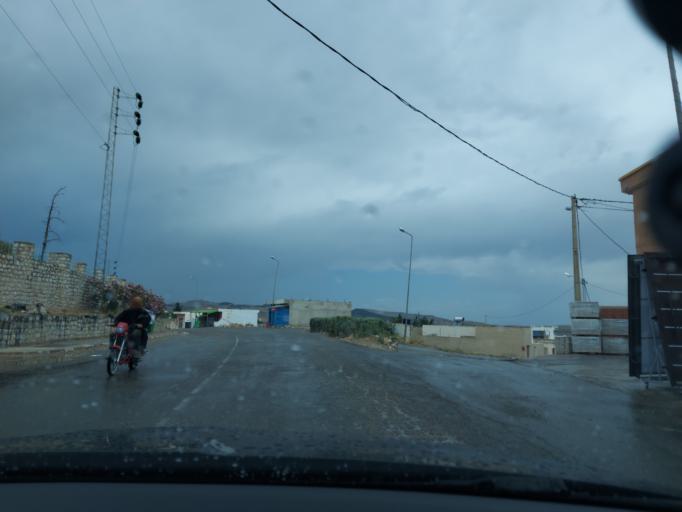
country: TN
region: Silyanah
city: Maktar
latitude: 35.8561
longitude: 9.2103
